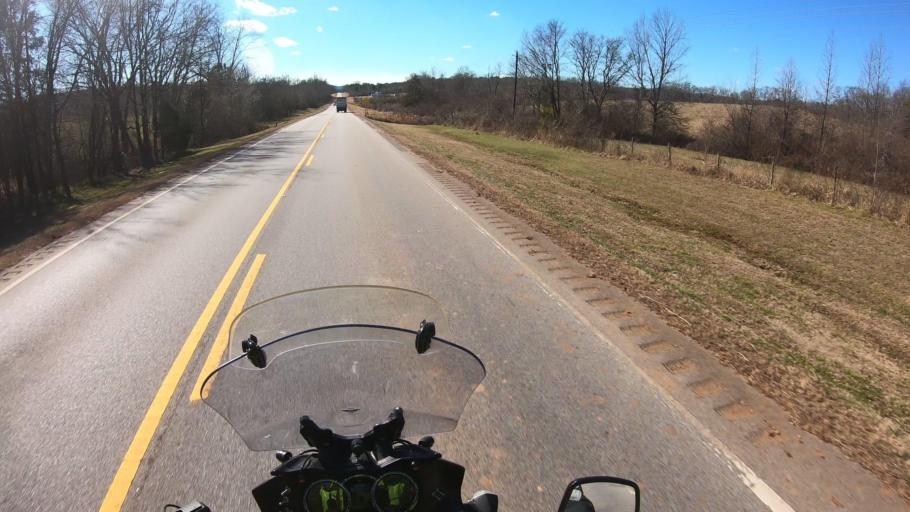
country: US
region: Alabama
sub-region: Calhoun County
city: Choccolocco
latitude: 33.4803
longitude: -85.6888
